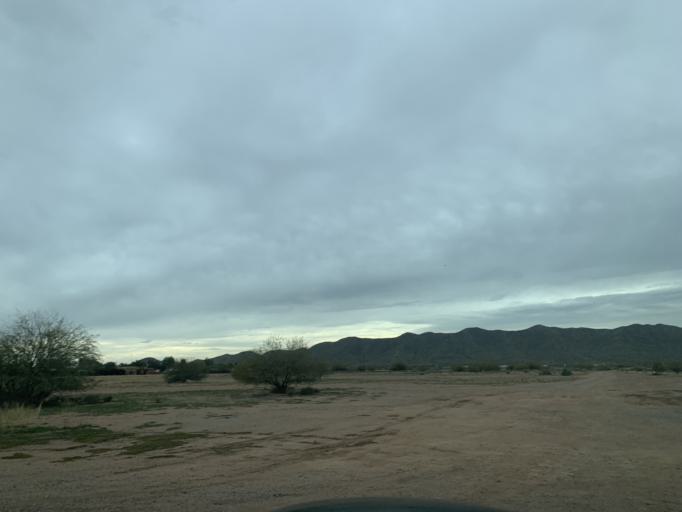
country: US
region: Arizona
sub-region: Pinal County
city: Arizona City
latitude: 32.8177
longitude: -111.6712
